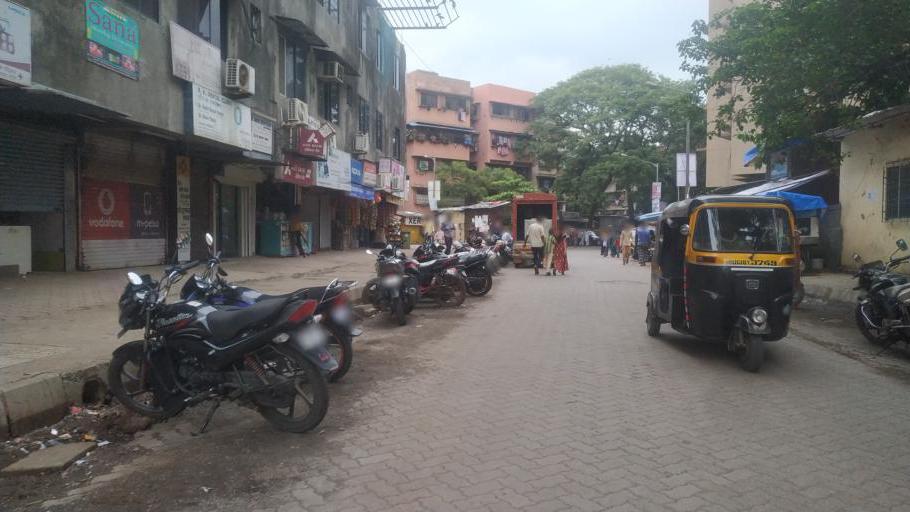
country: IN
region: Maharashtra
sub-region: Mumbai Suburban
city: Mumbai
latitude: 19.0717
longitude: 72.8837
